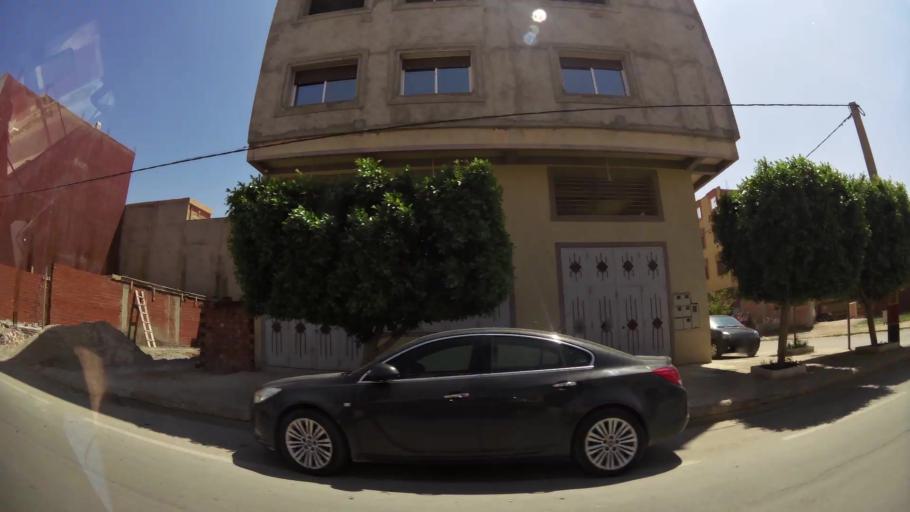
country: MA
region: Oriental
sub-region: Oujda-Angad
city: Oujda
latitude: 34.6962
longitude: -1.8848
